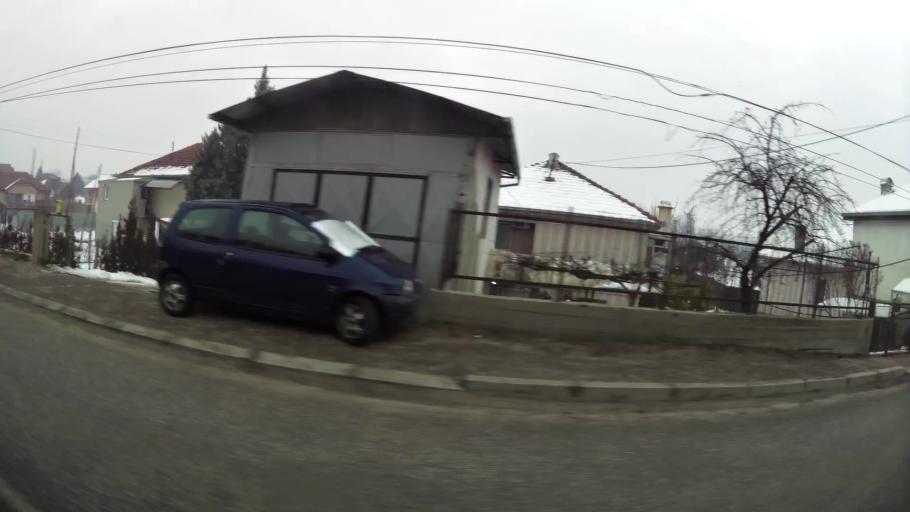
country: MK
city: Kondovo
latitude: 42.0438
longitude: 21.3465
